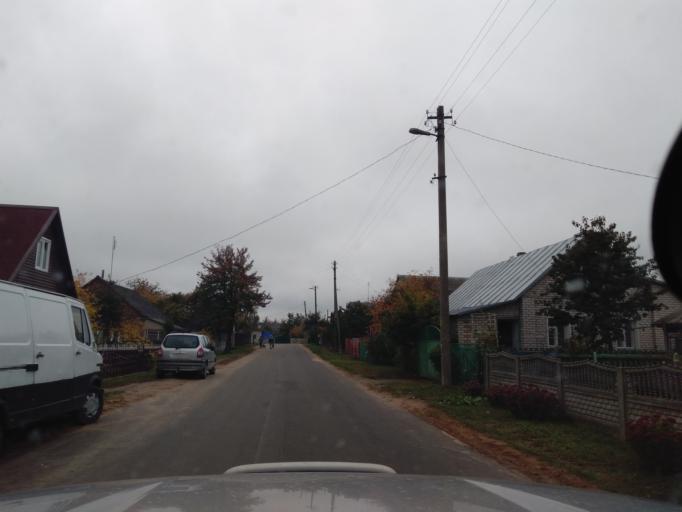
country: BY
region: Minsk
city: Kapyl'
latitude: 53.1419
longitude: 27.0924
